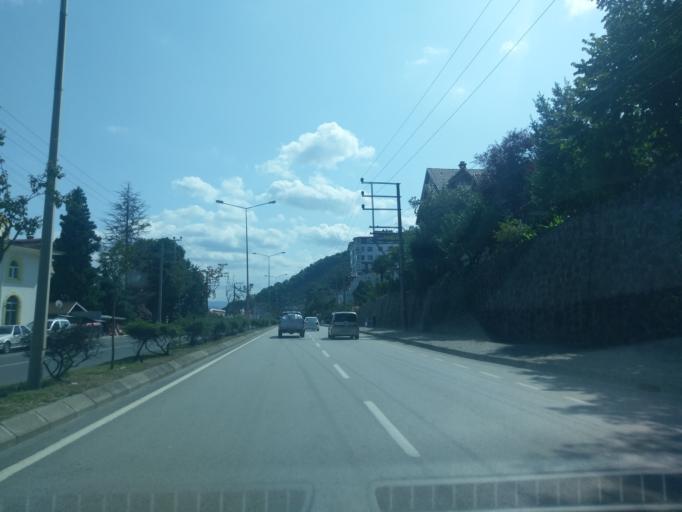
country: TR
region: Ordu
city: Ordu
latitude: 41.0039
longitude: 37.8704
